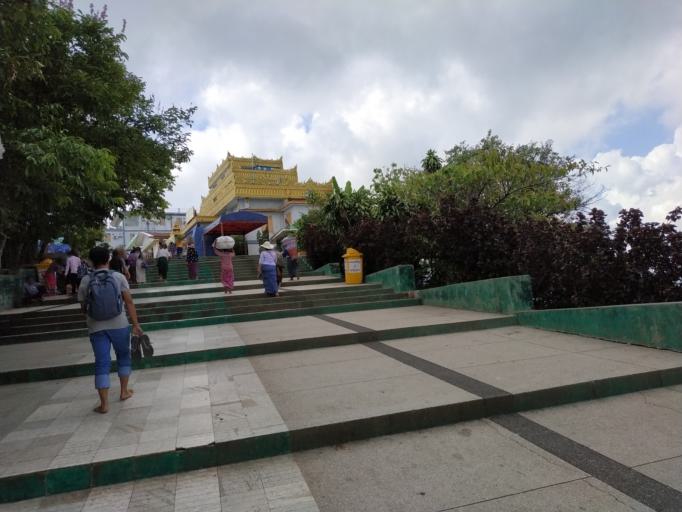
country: MM
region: Mon
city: Kyaikto
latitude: 17.4789
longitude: 97.1003
